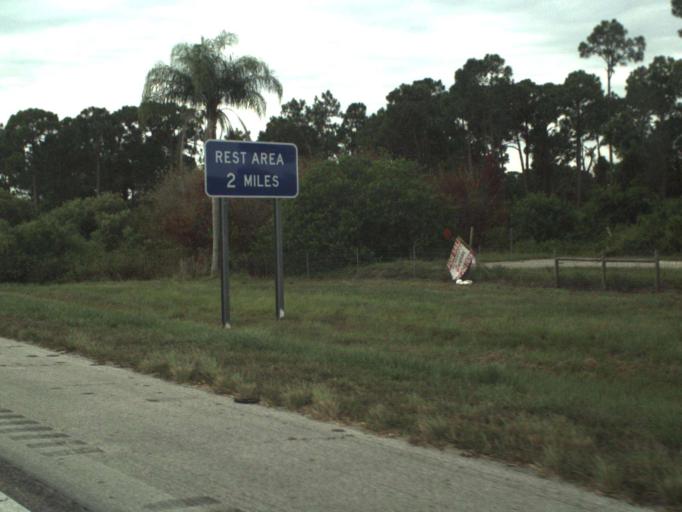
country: US
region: Florida
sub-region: Martin County
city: Palm City
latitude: 27.1427
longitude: -80.3722
